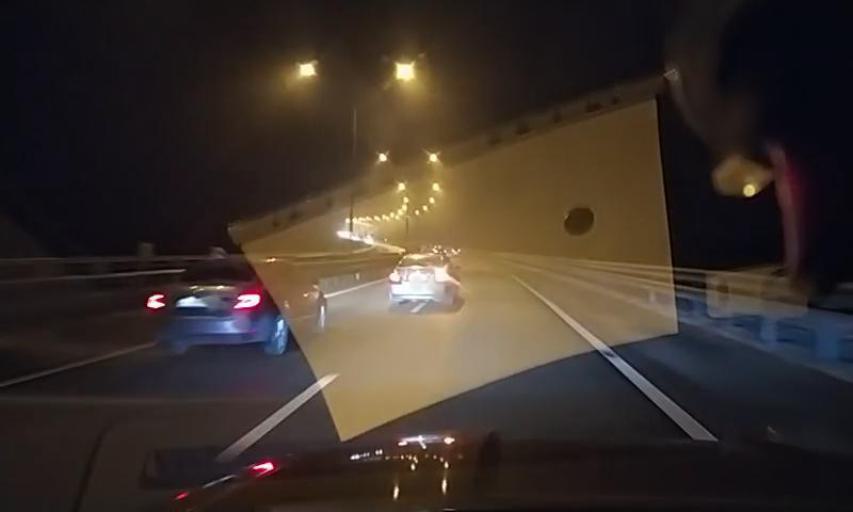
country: RU
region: Leningrad
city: Bugry
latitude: 60.1082
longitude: 30.3874
